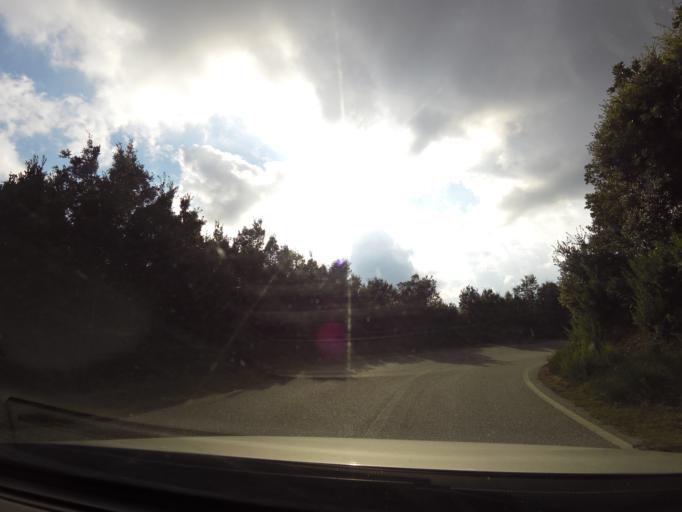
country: IT
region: Calabria
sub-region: Provincia di Vibo-Valentia
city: Nardodipace
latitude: 38.4766
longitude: 16.3863
